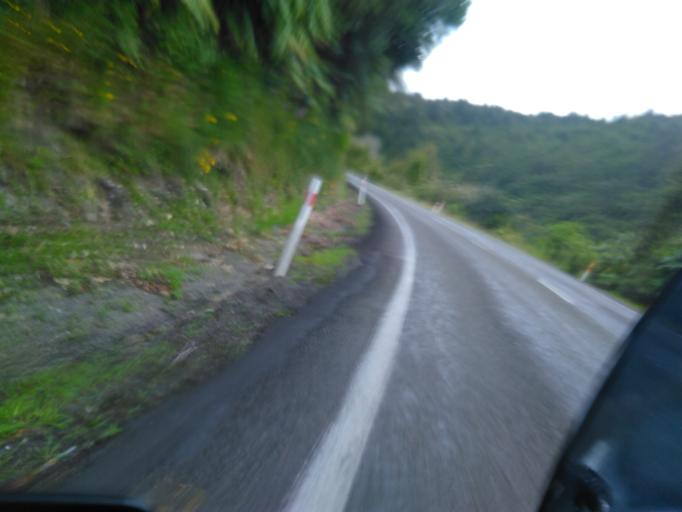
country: NZ
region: Bay of Plenty
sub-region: Opotiki District
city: Opotiki
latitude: -38.2371
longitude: 177.3081
